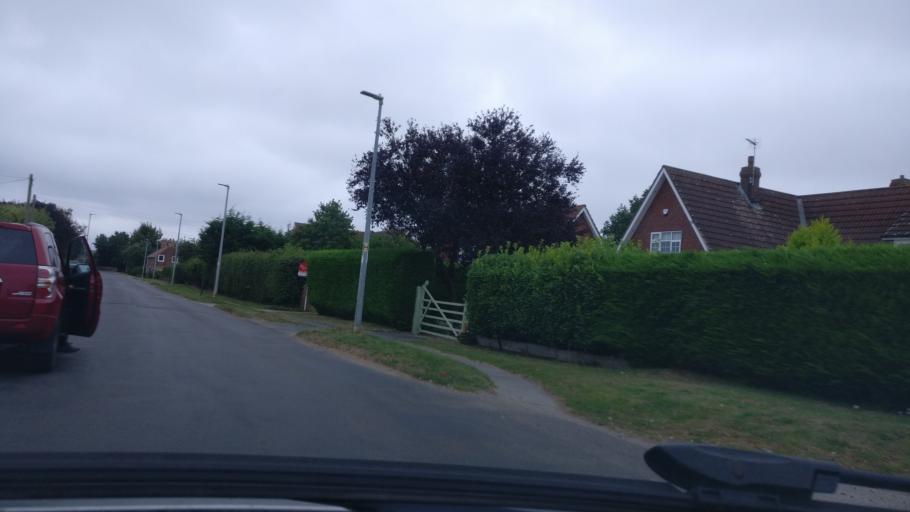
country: GB
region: England
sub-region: East Riding of Yorkshire
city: Leven
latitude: 53.8927
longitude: -0.3230
